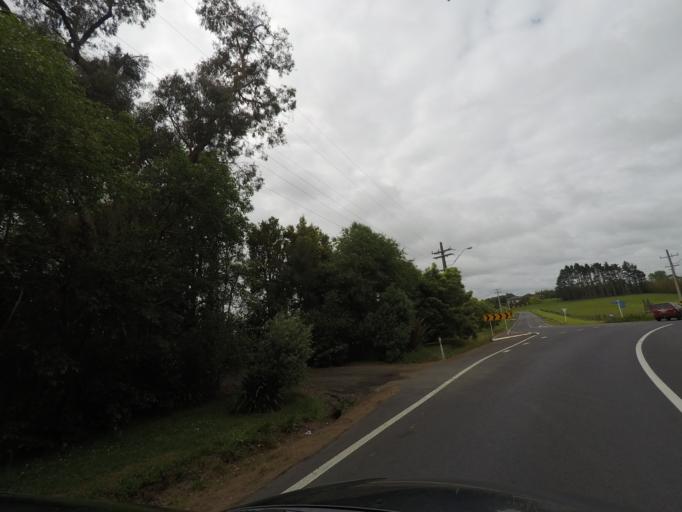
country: NZ
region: Auckland
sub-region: Auckland
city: Rosebank
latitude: -36.7994
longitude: 174.5738
